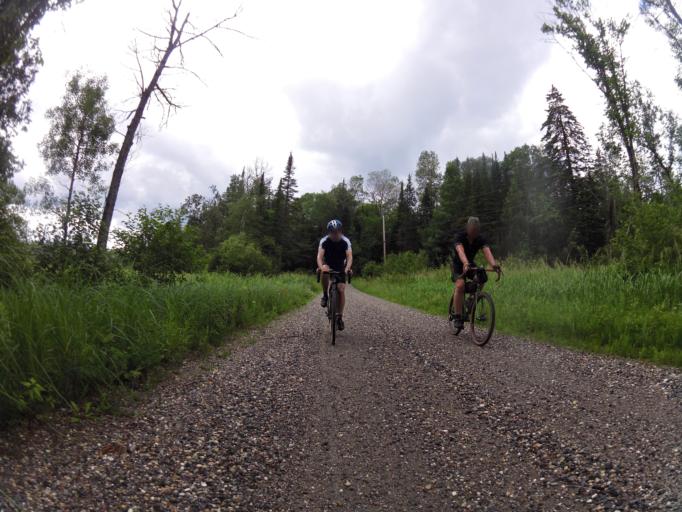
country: CA
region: Ontario
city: Renfrew
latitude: 45.0730
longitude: -76.7488
